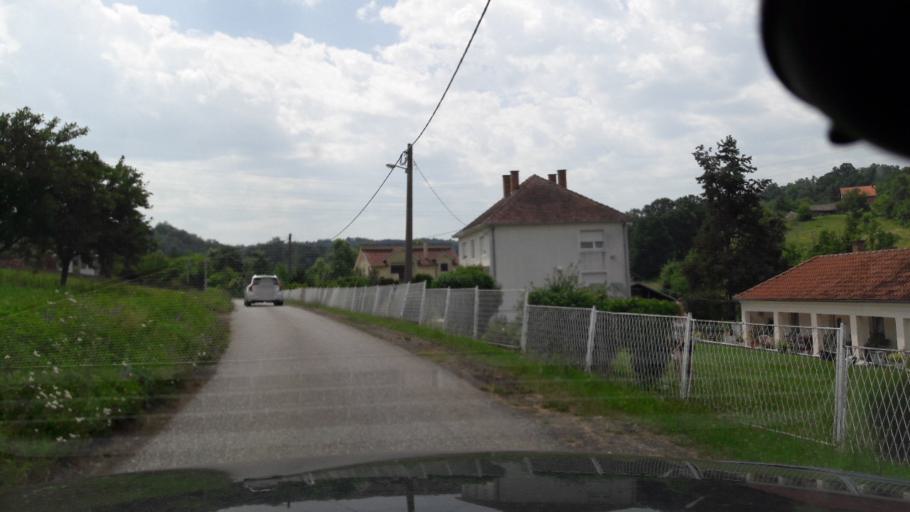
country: RS
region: Central Serbia
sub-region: Belgrade
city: Sopot
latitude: 44.6290
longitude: 20.5960
